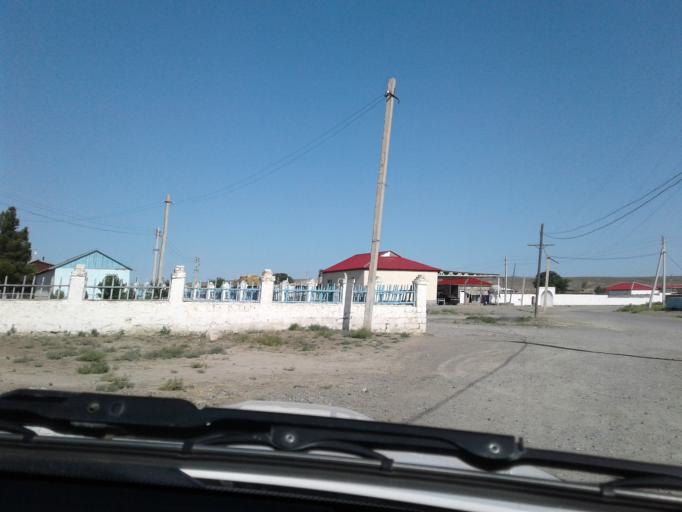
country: TM
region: Balkan
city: Serdar
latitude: 38.7123
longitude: 56.3389
